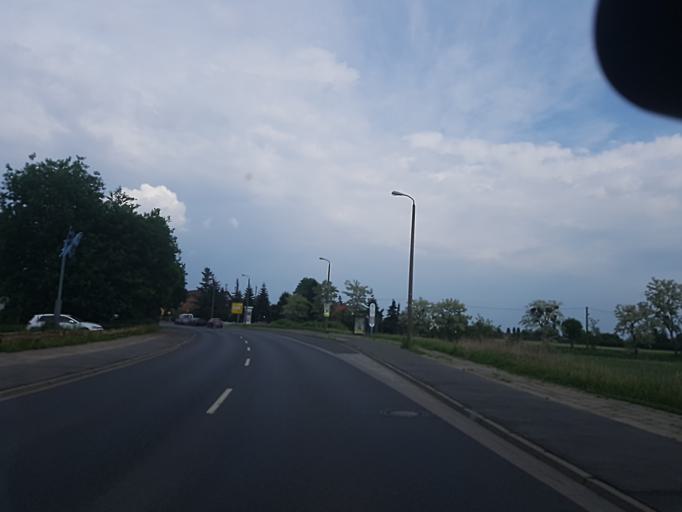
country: DE
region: Saxony-Anhalt
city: Wittenburg
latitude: 51.8772
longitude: 12.6029
